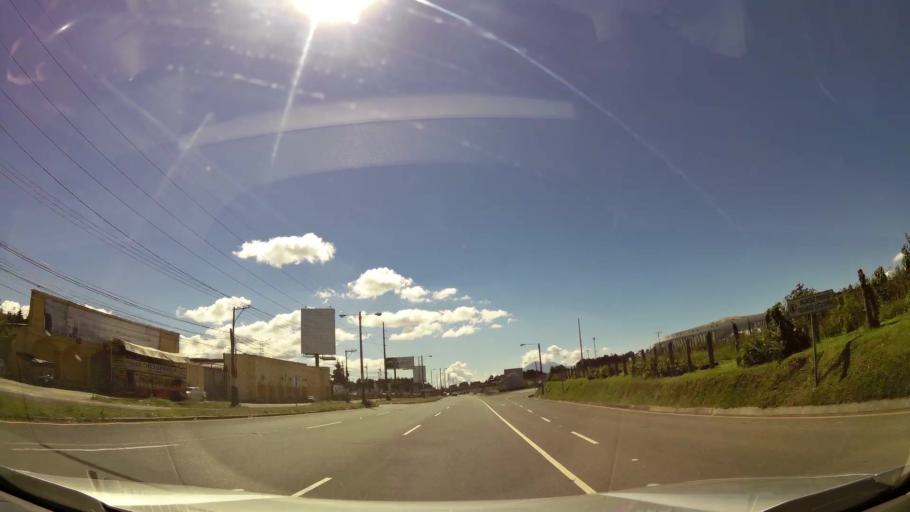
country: GT
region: Guatemala
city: Santa Catarina Pinula
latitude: 14.5129
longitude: -90.4762
